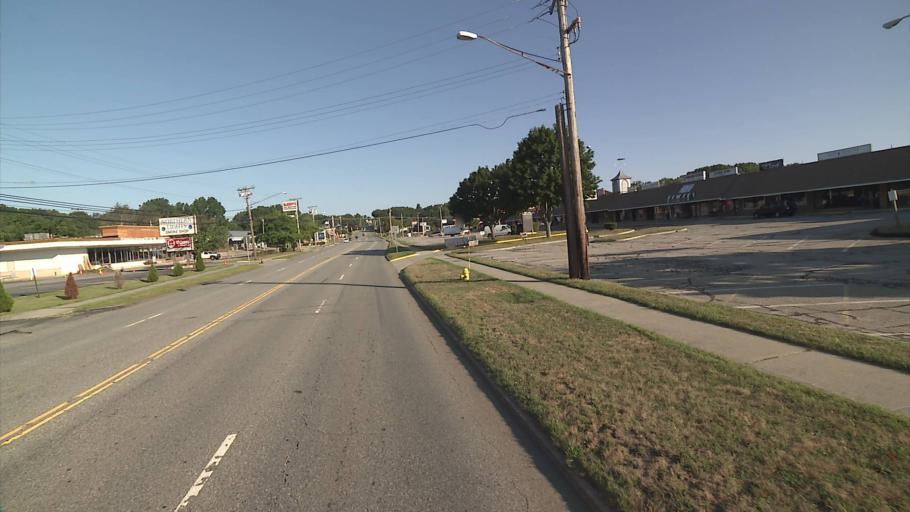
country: US
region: Connecticut
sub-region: New London County
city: Long Hill
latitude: 41.3477
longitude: -72.0529
